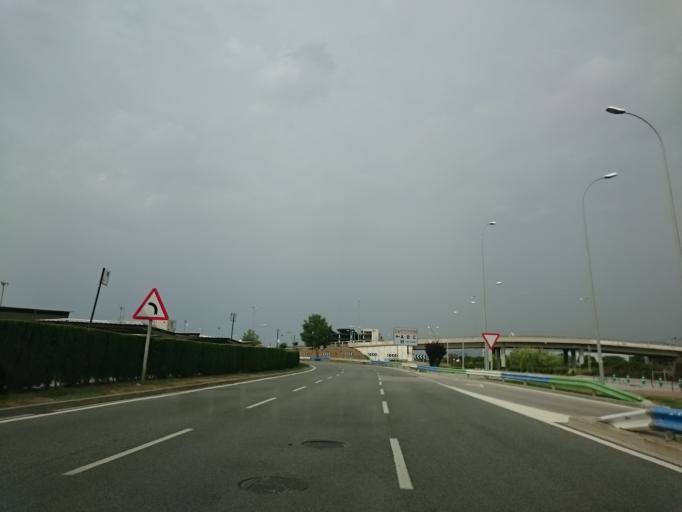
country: ES
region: Catalonia
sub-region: Provincia de Barcelona
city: El Prat de Llobregat
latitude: 41.3027
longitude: 2.0701
